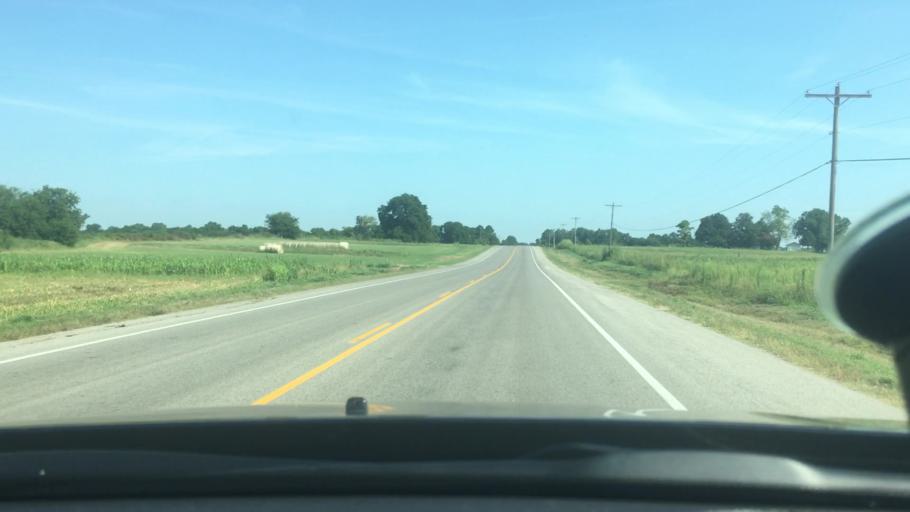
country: US
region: Oklahoma
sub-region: Garvin County
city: Wynnewood
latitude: 34.6591
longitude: -97.2027
